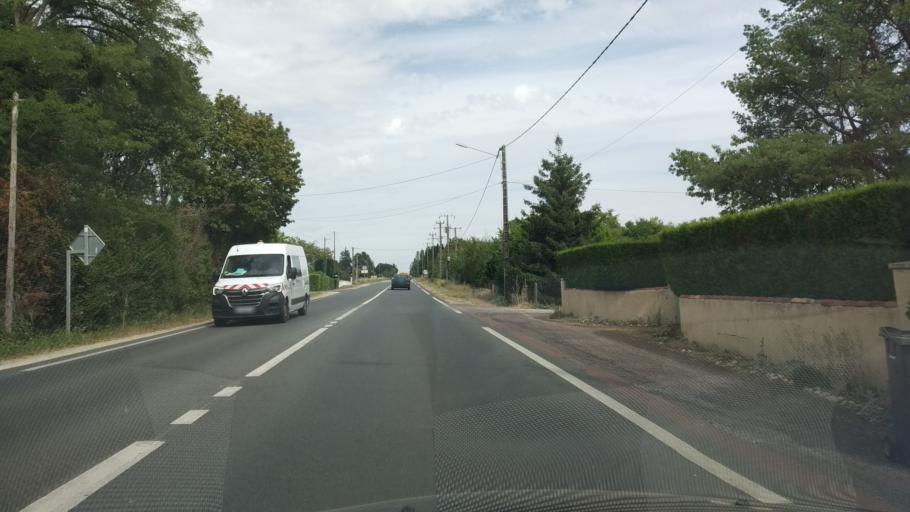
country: FR
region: Poitou-Charentes
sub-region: Departement de la Vienne
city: Mignaloux-Beauvoir
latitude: 46.5616
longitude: 0.4303
